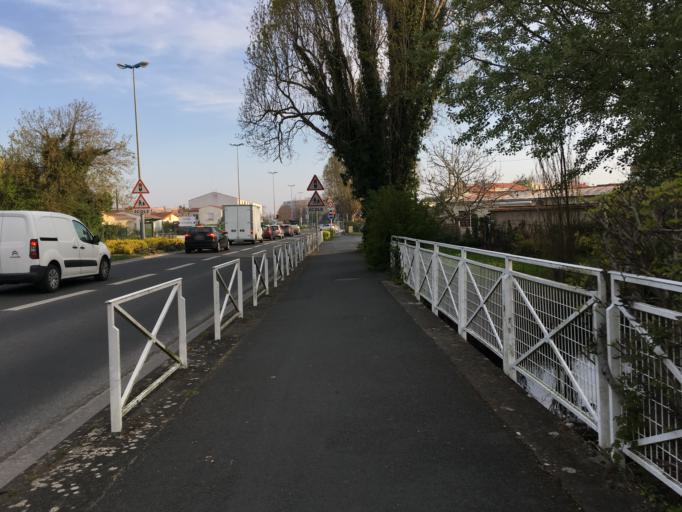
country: FR
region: Poitou-Charentes
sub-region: Departement de la Charente-Maritime
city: La Rochelle
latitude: 46.1724
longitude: -1.1503
